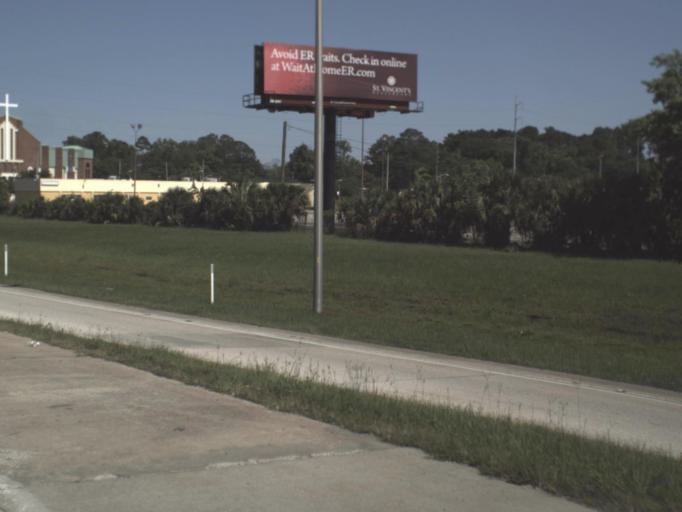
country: US
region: Florida
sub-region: Duval County
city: Jacksonville
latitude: 30.3154
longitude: -81.7498
